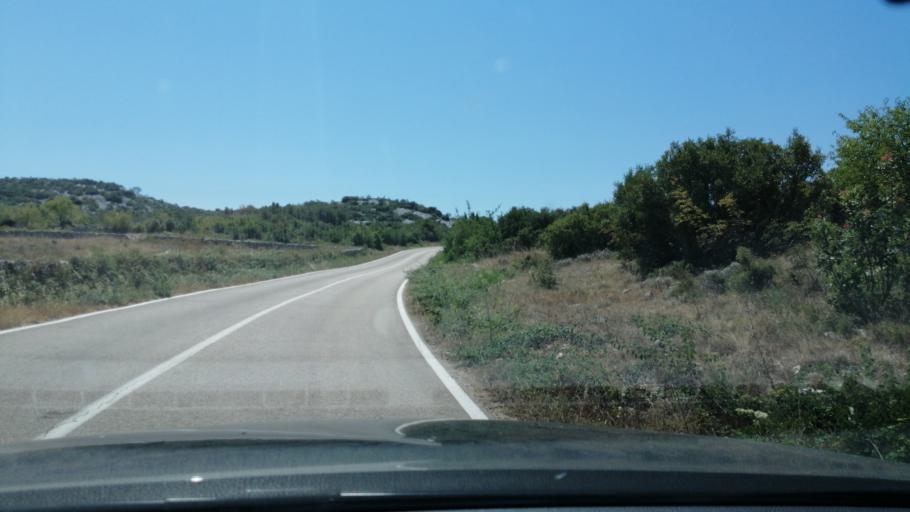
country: HR
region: Sibensko-Kniniska
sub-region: Grad Sibenik
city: Pirovac
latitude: 43.8592
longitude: 15.6927
